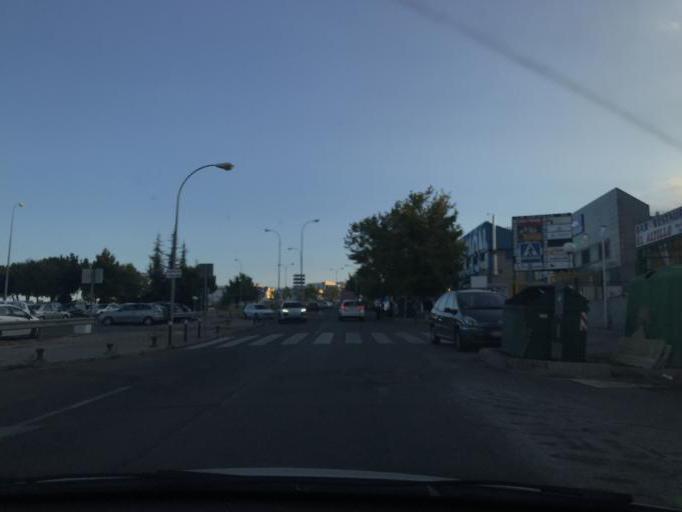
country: ES
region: Madrid
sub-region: Provincia de Madrid
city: Alcobendas
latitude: 40.5352
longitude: -3.6568
